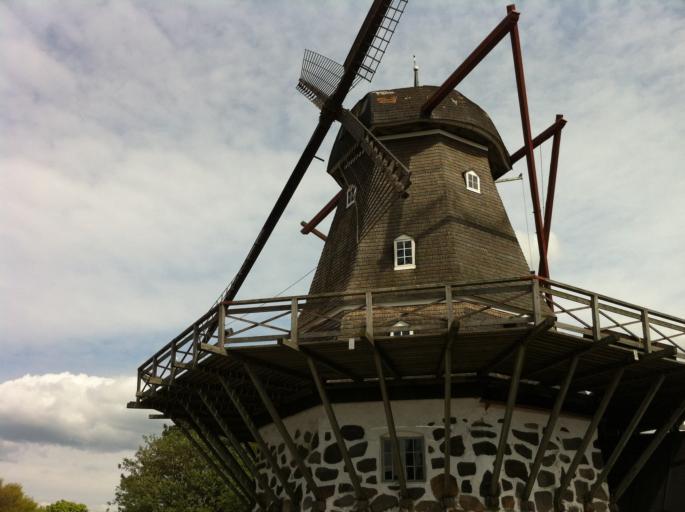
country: SE
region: Skane
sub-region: Hoganas Kommun
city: Hoganas
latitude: 56.1445
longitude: 12.5773
